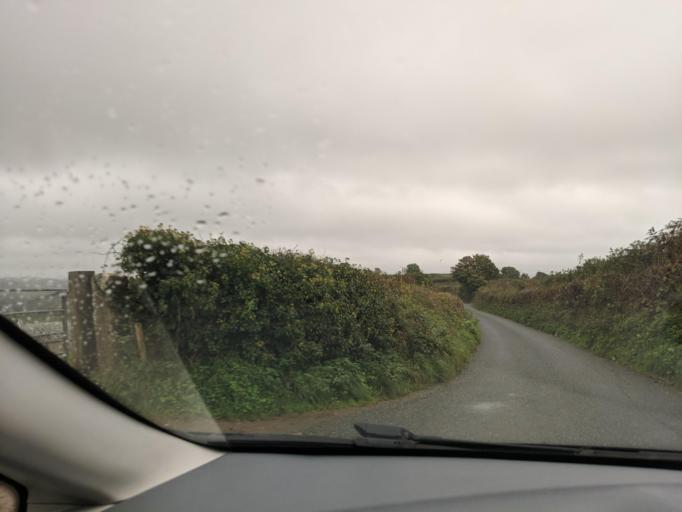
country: GB
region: England
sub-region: Cornwall
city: Saltash
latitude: 50.4541
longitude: -4.2494
